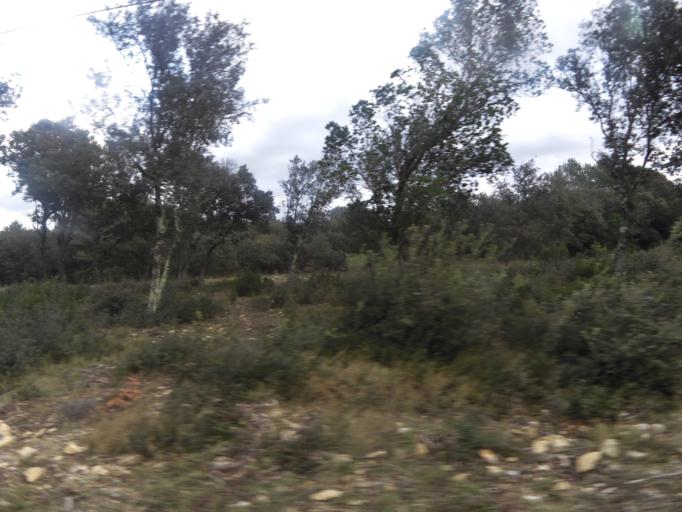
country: FR
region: Languedoc-Roussillon
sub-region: Departement du Gard
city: Saint-Mamert-du-Gard
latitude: 43.8513
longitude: 4.1890
